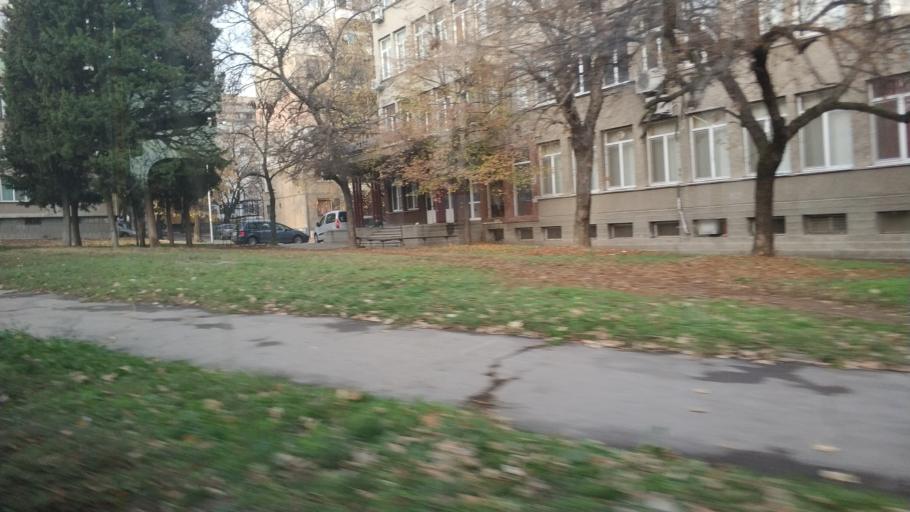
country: BG
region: Stara Zagora
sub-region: Obshtina Stara Zagora
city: Stara Zagora
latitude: 42.4190
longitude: 25.6204
